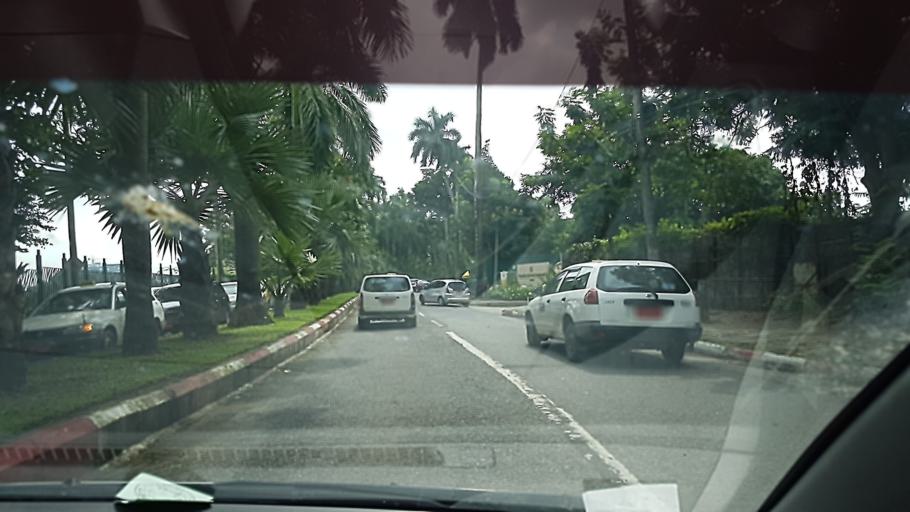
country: MM
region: Yangon
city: Yangon
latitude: 16.7933
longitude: 96.1627
